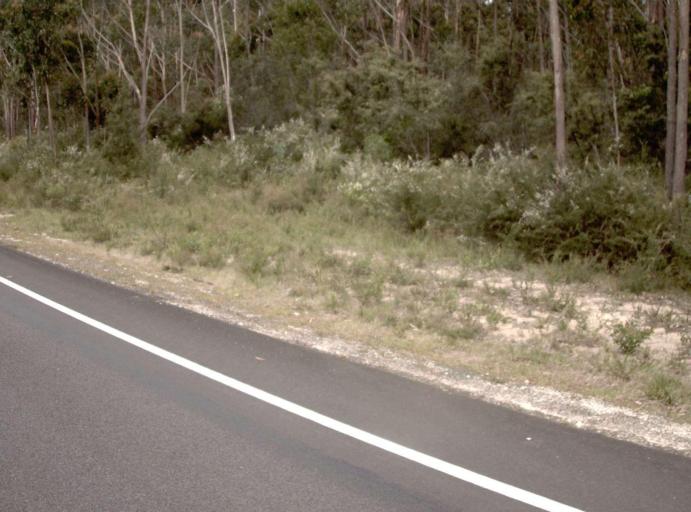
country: AU
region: New South Wales
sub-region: Bega Valley
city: Eden
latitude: -37.5093
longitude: 149.5162
